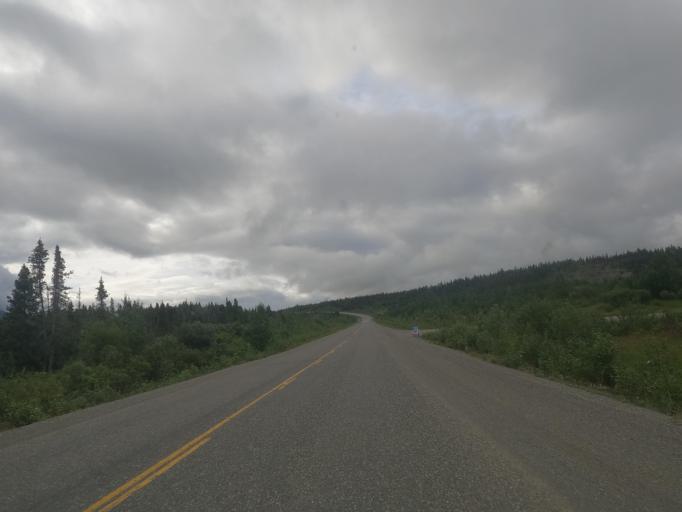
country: CA
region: Yukon
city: Haines Junction
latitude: 59.9957
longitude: -136.8451
